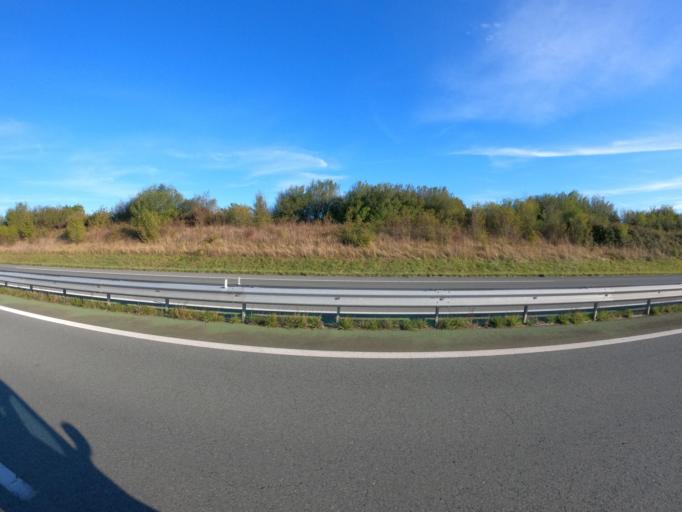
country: FR
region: Pays de la Loire
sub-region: Departement de Maine-et-Loire
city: Trementines
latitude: 47.1662
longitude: -0.8088
